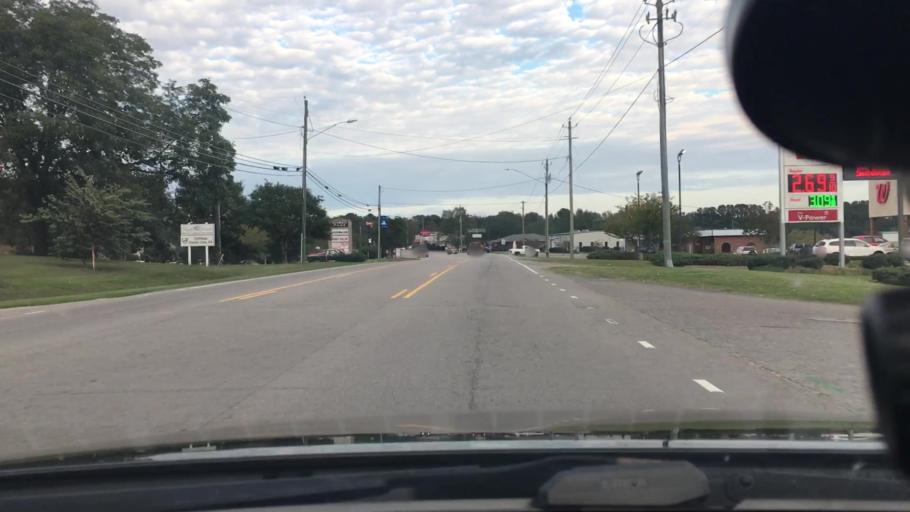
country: US
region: North Carolina
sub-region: Moore County
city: Carthage
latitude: 35.3409
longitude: -79.4043
